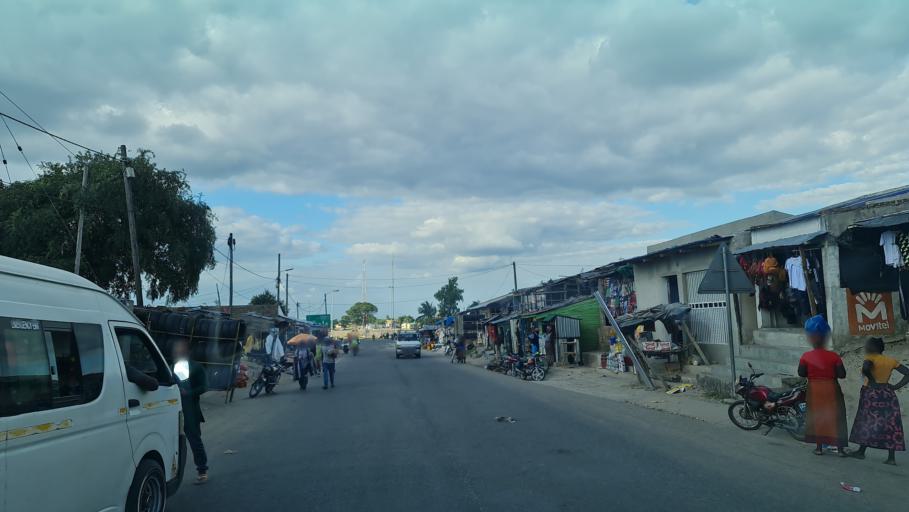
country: MZ
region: Manica
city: Chimoio
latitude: -19.2092
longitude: 33.9295
